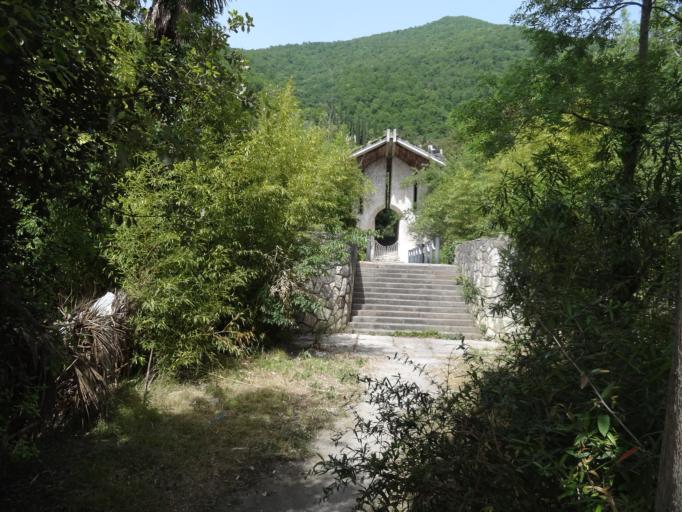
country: GE
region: Abkhazia
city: Gagra
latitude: 43.3235
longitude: 40.2312
